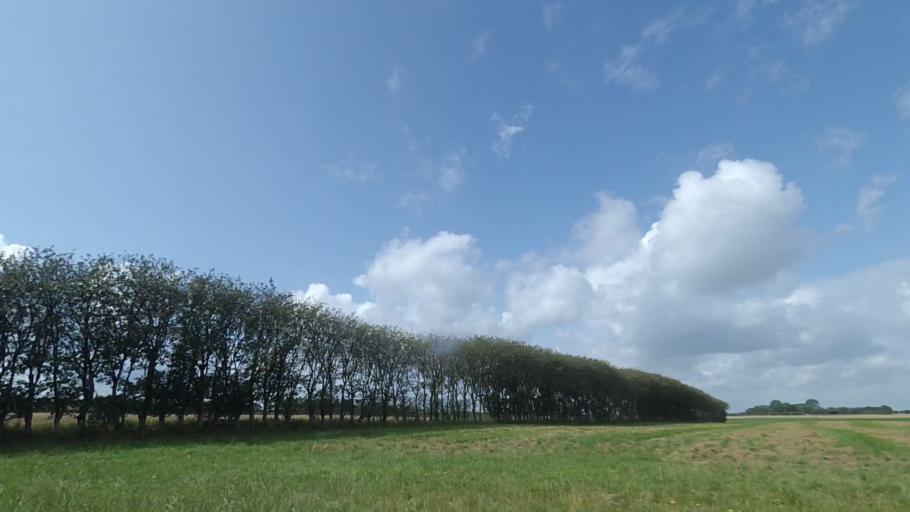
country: DK
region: Central Jutland
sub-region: Syddjurs Kommune
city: Ryomgard
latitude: 56.4713
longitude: 10.5104
